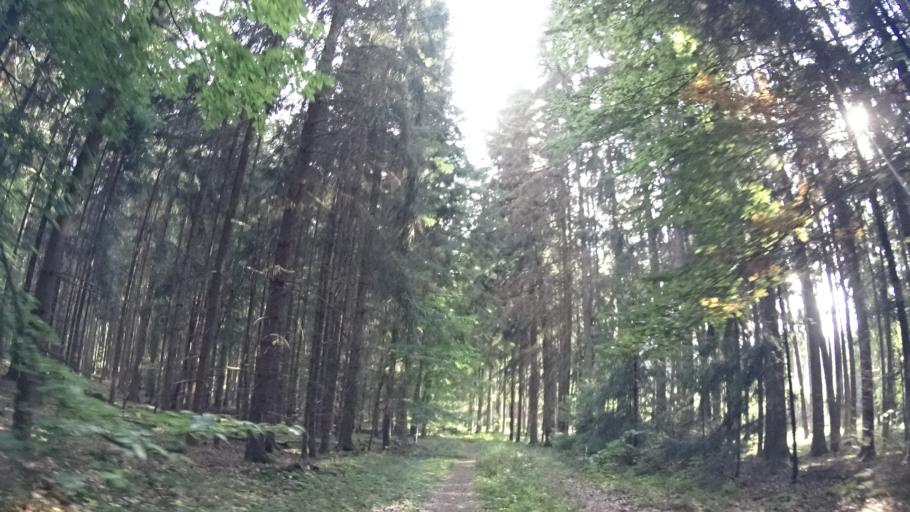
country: DE
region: Bavaria
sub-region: Lower Bavaria
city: Riedenburg
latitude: 48.9194
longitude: 11.6407
